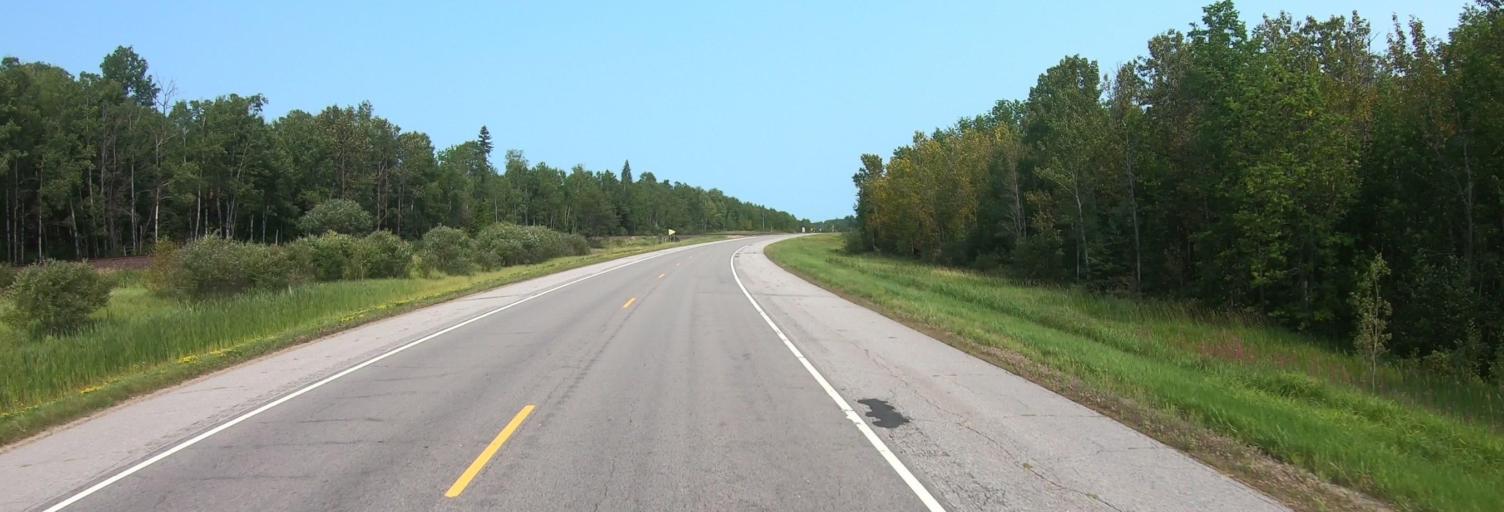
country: CA
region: Ontario
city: Fort Frances
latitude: 48.2302
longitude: -92.9262
